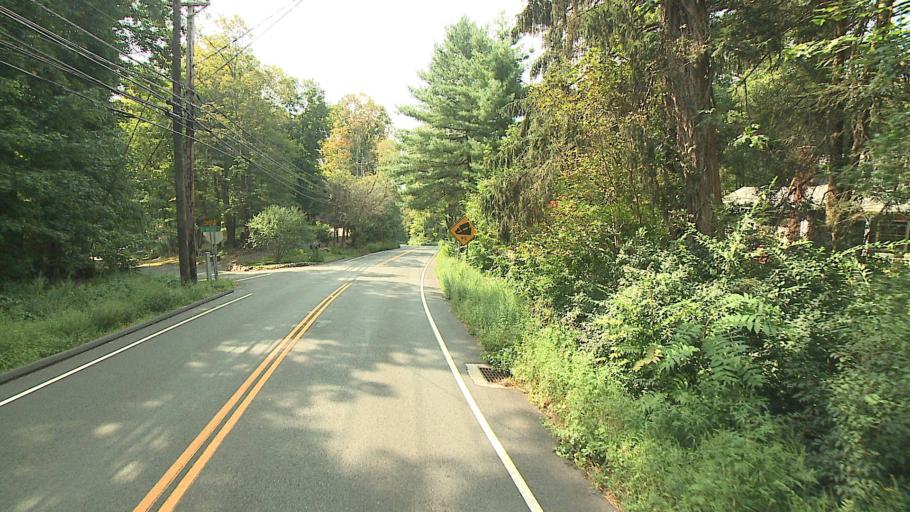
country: US
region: Connecticut
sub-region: Fairfield County
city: Georgetown
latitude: 41.2992
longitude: -73.3883
